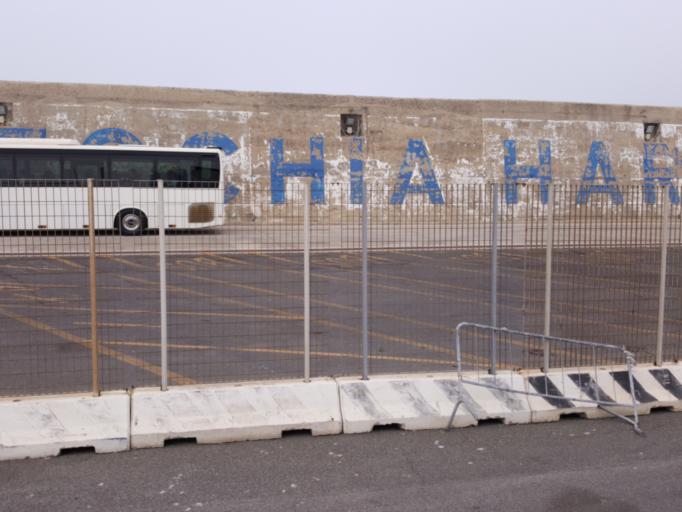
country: IT
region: Latium
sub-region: Citta metropolitana di Roma Capitale
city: Civitavecchia
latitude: 42.0993
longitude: 11.7734
